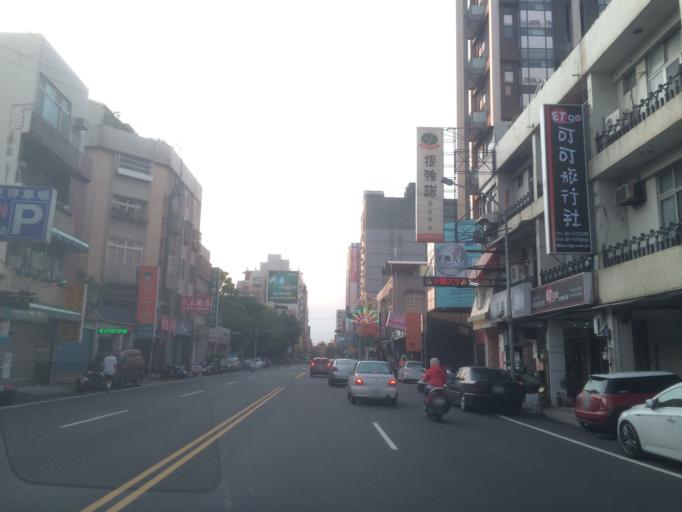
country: TW
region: Taiwan
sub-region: Hsinchu
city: Hsinchu
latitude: 24.7988
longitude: 120.9626
